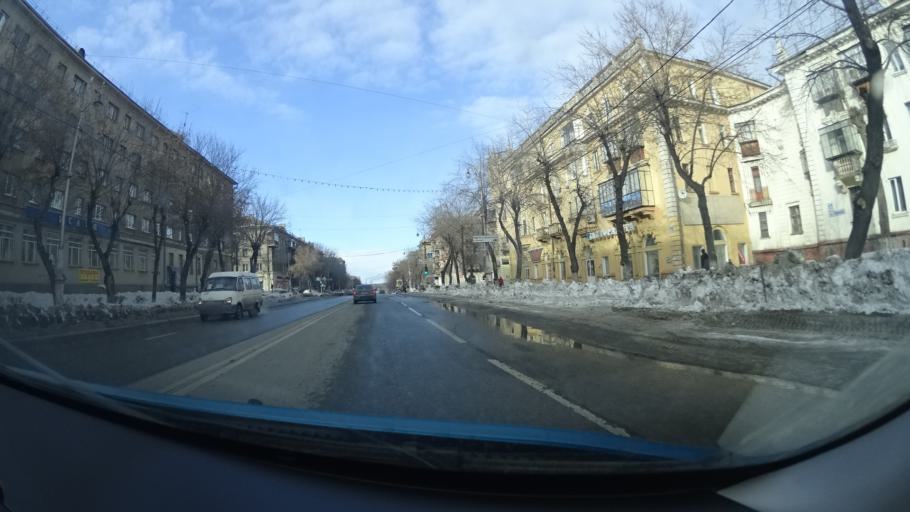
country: RU
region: Chelyabinsk
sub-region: Gorod Magnitogorsk
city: Magnitogorsk
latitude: 53.4312
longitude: 58.9837
